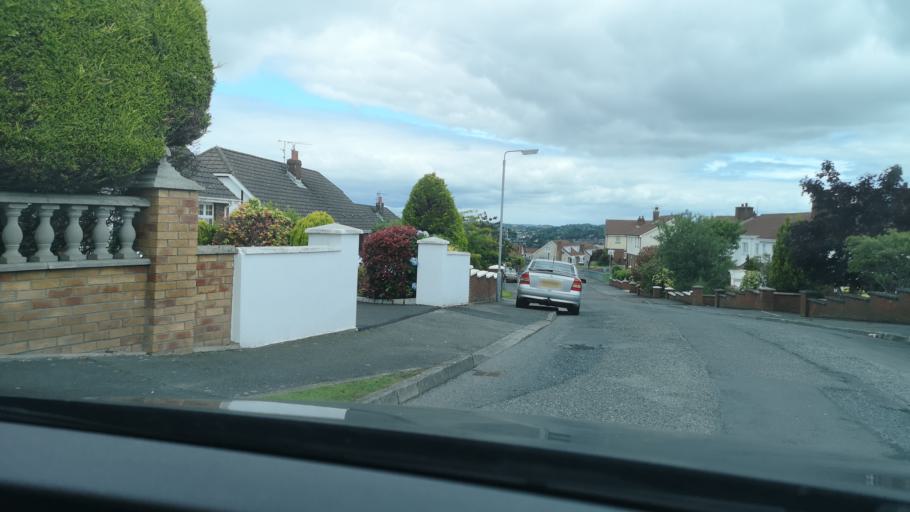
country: GB
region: Northern Ireland
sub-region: Newry and Mourne District
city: Newry
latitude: 54.1734
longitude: -6.3280
